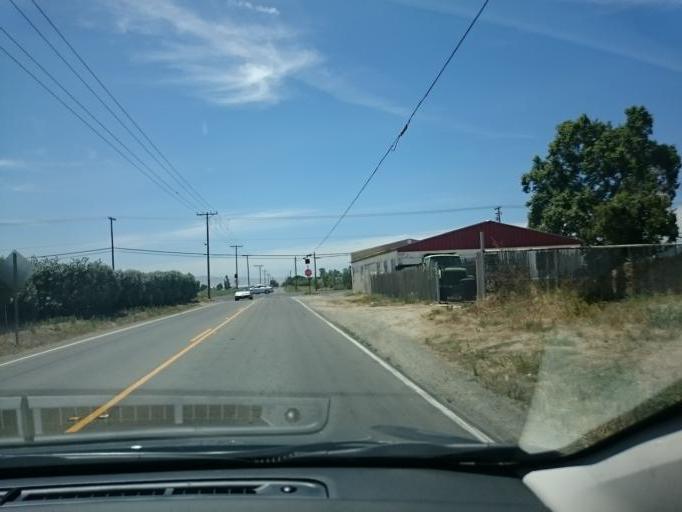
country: US
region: California
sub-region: Stanislaus County
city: Bret Harte
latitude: 37.5513
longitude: -120.9927
